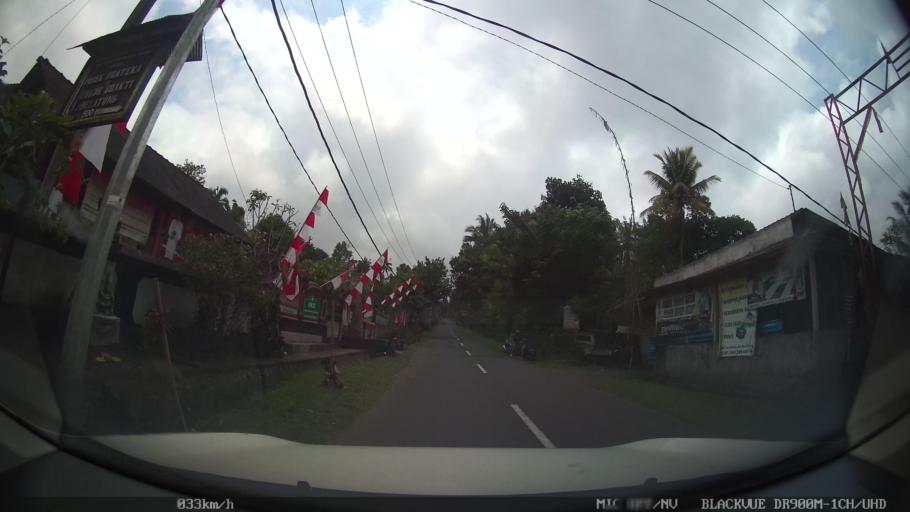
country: ID
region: Bali
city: Banjar Geriana Kangin
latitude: -8.4071
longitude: 115.4394
